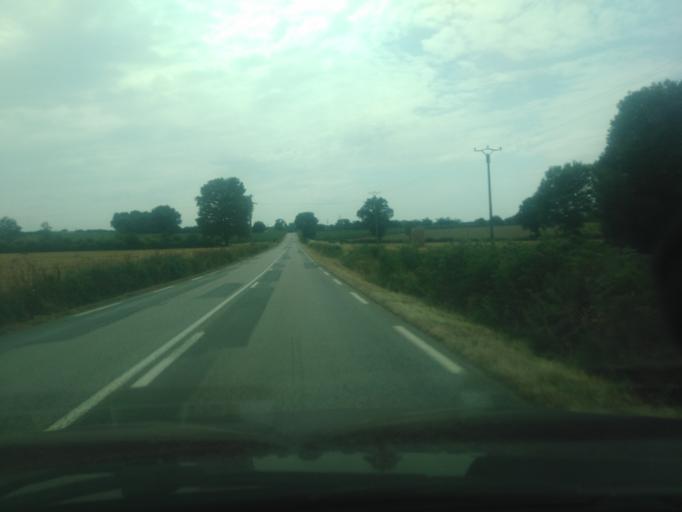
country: FR
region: Poitou-Charentes
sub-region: Departement des Deux-Sevres
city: Moncoutant
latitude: 46.6330
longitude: -0.5437
